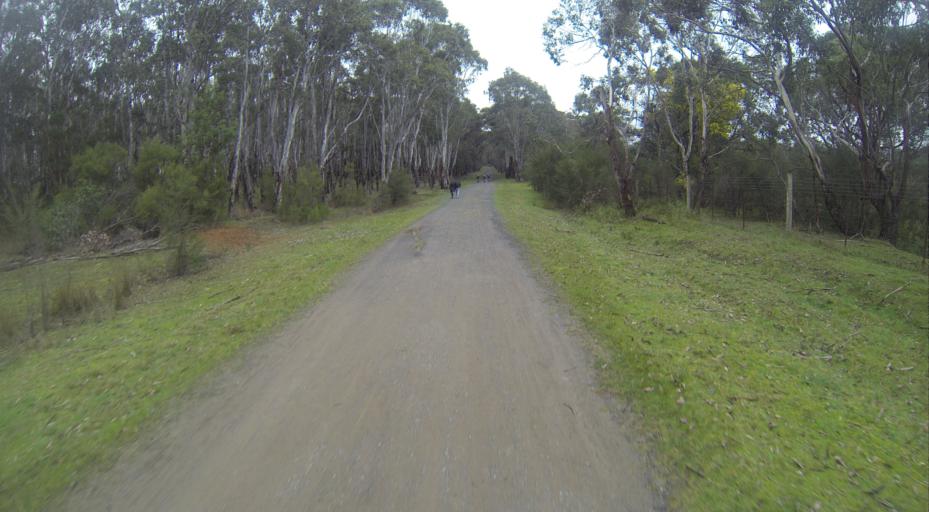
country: AU
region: Victoria
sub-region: Casey
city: Narre Warren North
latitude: -37.9616
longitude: 145.3059
